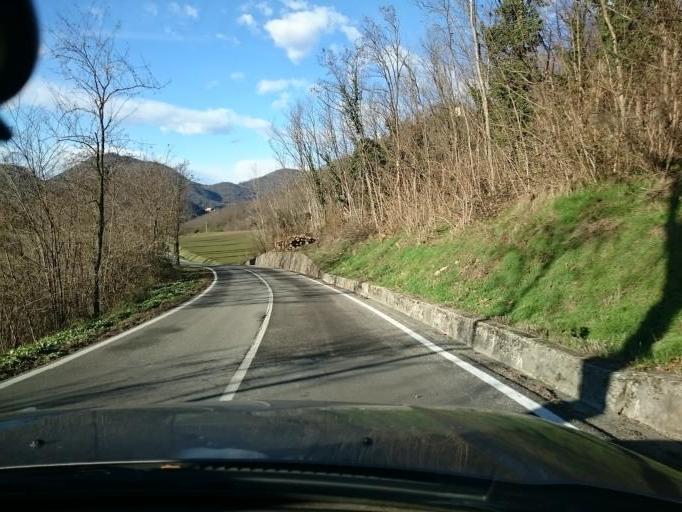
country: IT
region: Veneto
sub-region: Provincia di Padova
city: Treponti
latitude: 45.3341
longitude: 11.6832
